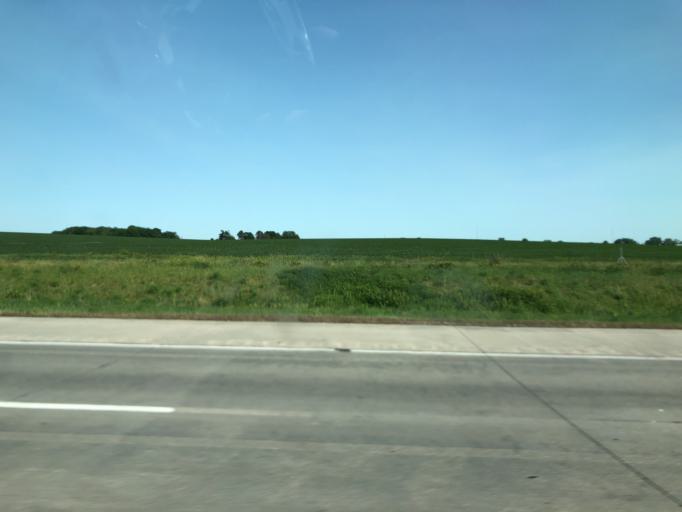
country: US
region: Nebraska
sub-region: Saunders County
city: Ashland
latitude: 40.9602
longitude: -96.4062
